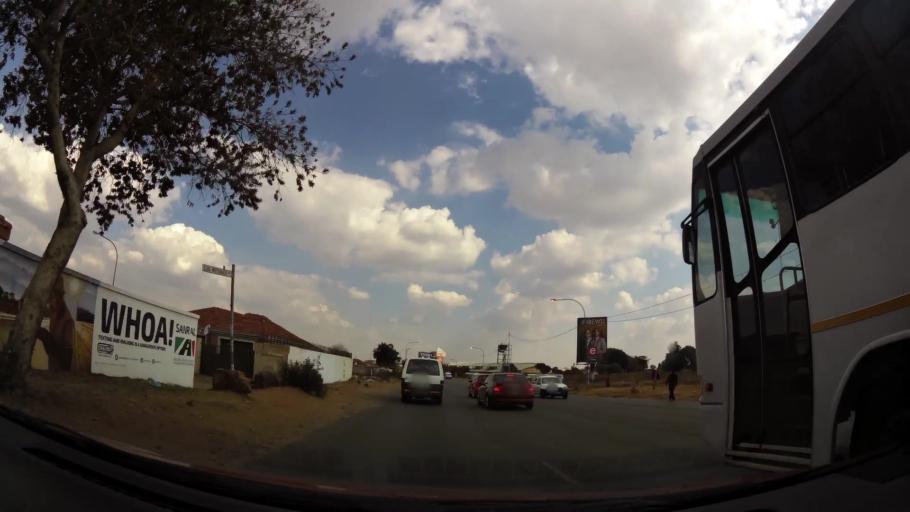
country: ZA
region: Gauteng
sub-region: City of Johannesburg Metropolitan Municipality
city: Roodepoort
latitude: -26.2077
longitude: 27.8716
